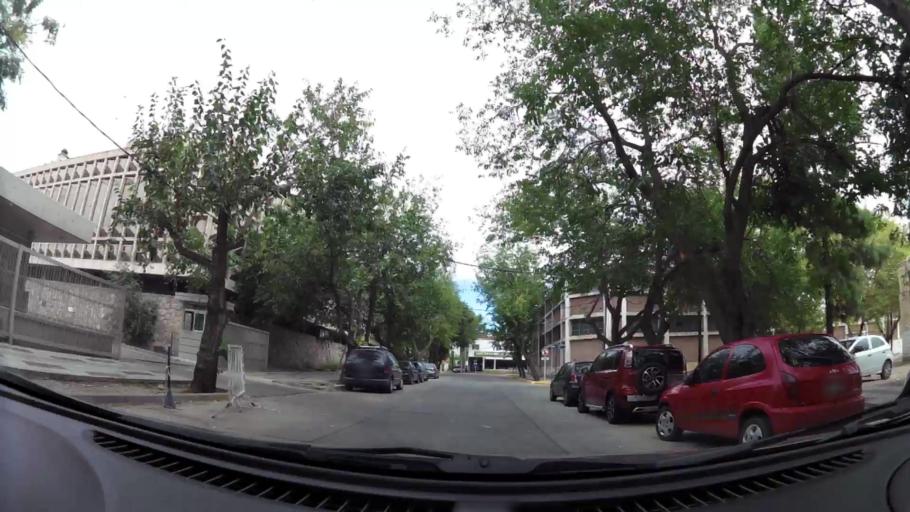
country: AR
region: Mendoza
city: Mendoza
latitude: -32.8980
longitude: -68.8505
